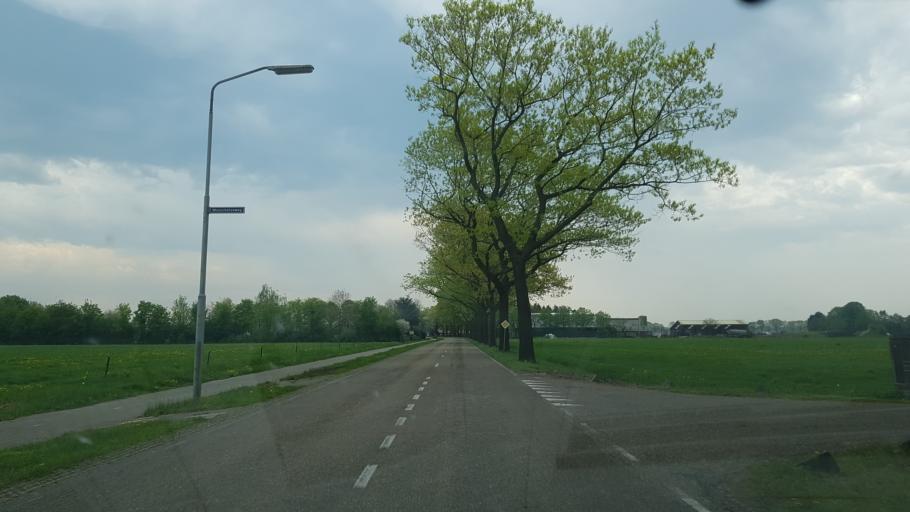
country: NL
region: North Brabant
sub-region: Gemeente Someren
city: Someren
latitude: 51.3679
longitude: 5.6999
